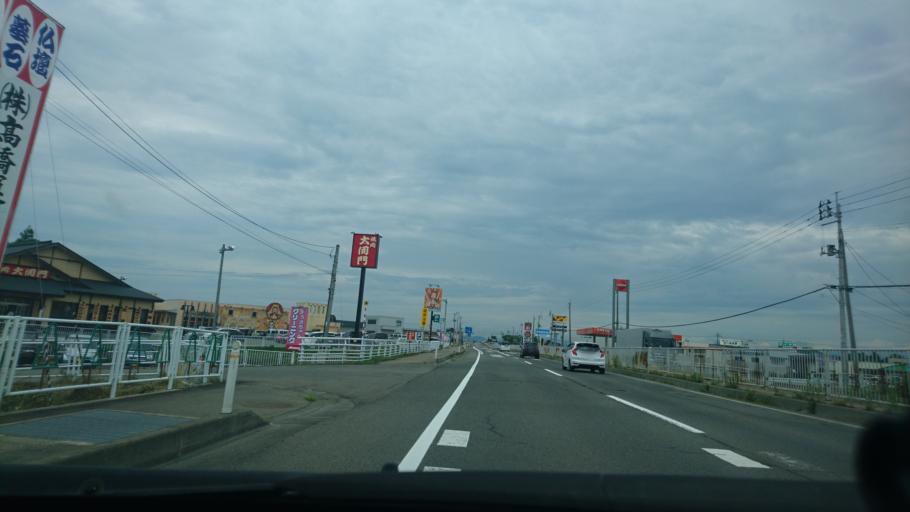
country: JP
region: Akita
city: Omagari
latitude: 39.4561
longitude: 140.4972
